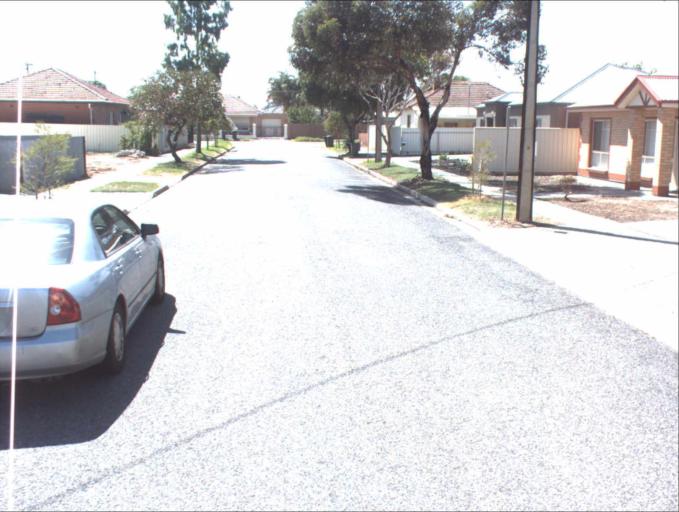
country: AU
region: South Australia
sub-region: Charles Sturt
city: Woodville
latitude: -34.8777
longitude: 138.5667
